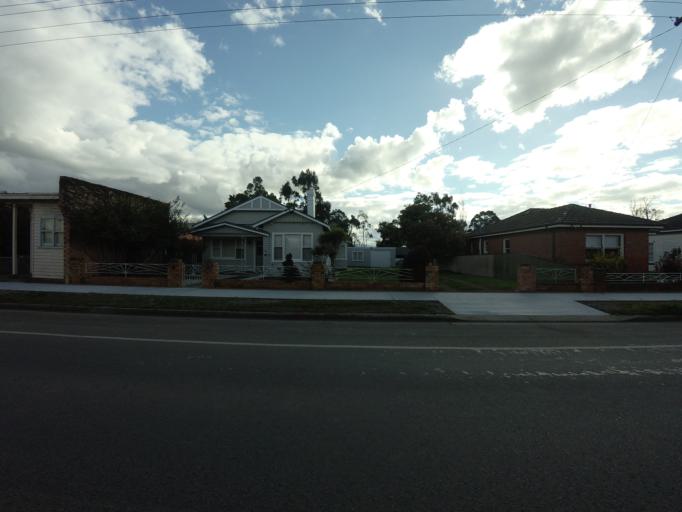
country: AU
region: Tasmania
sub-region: Northern Midlands
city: Longford
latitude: -41.6862
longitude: 147.0803
